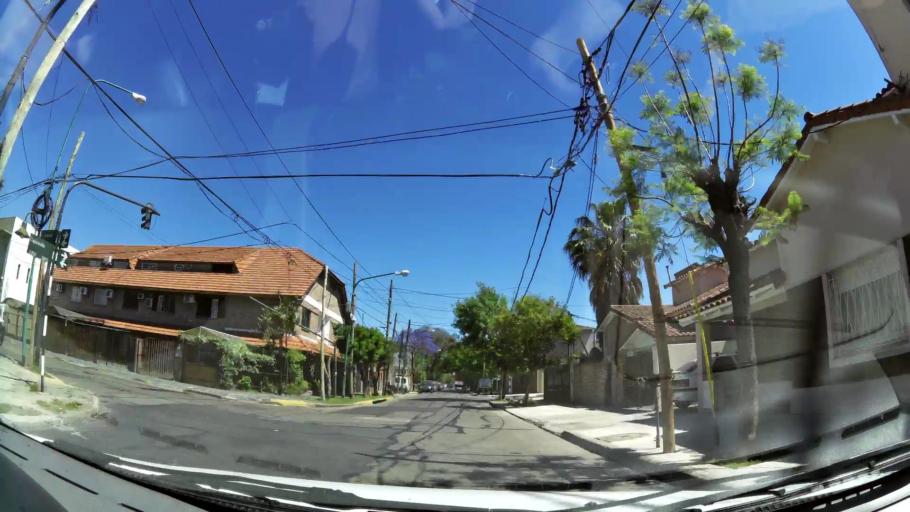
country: AR
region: Buenos Aires
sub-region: Partido de General San Martin
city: General San Martin
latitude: -34.5282
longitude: -58.5449
